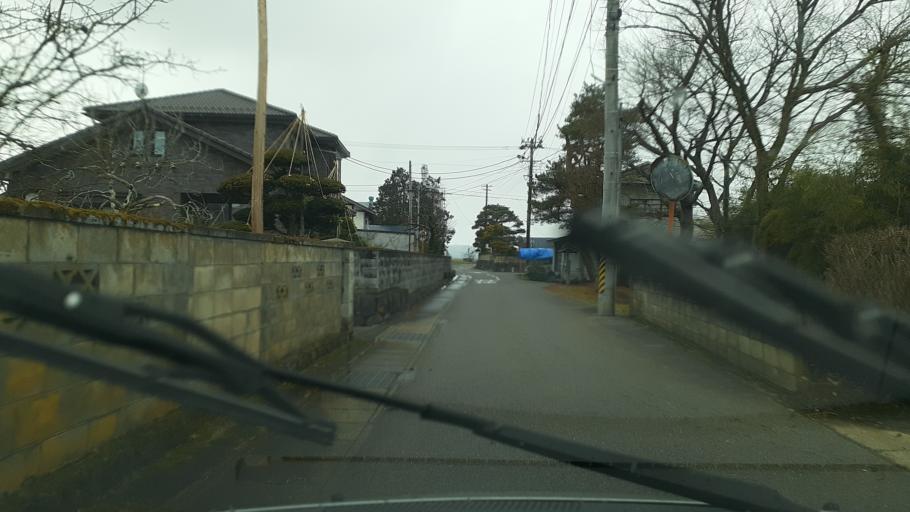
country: JP
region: Fukushima
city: Kitakata
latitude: 37.5593
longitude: 139.8851
